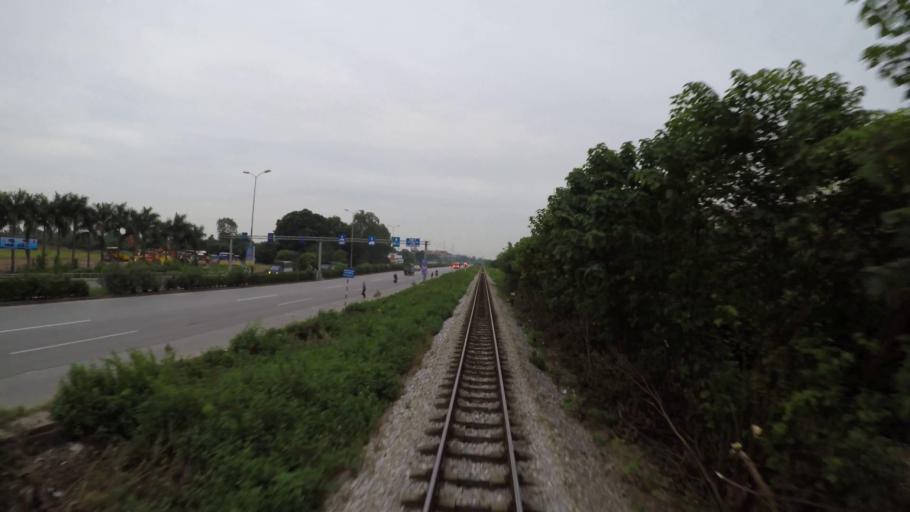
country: VN
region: Ha Noi
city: Trau Quy
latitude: 21.0142
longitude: 105.9477
